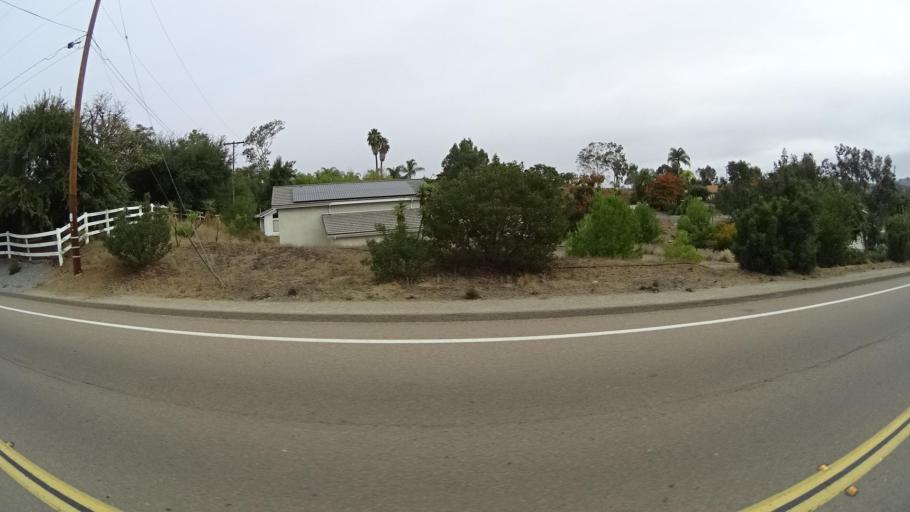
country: US
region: California
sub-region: San Diego County
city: Rancho San Diego
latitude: 32.7711
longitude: -116.9364
